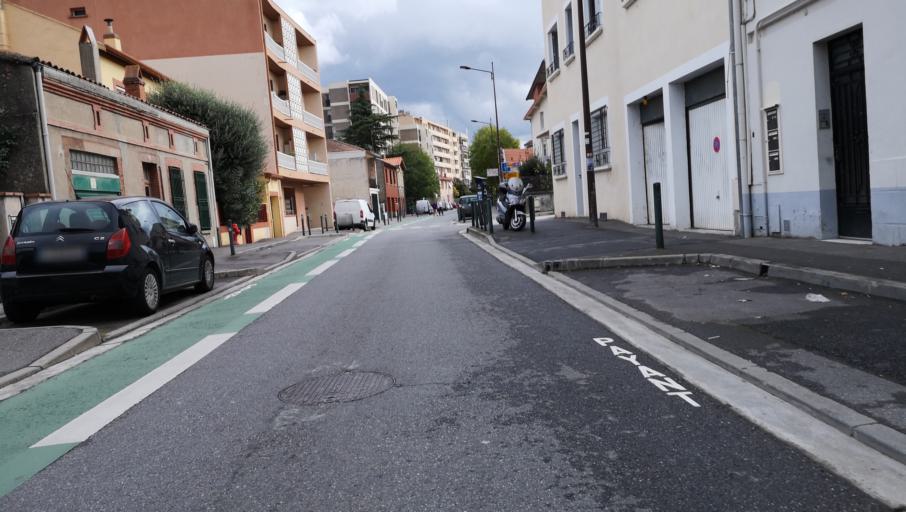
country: FR
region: Midi-Pyrenees
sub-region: Departement de la Haute-Garonne
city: Toulouse
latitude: 43.6006
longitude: 1.4242
